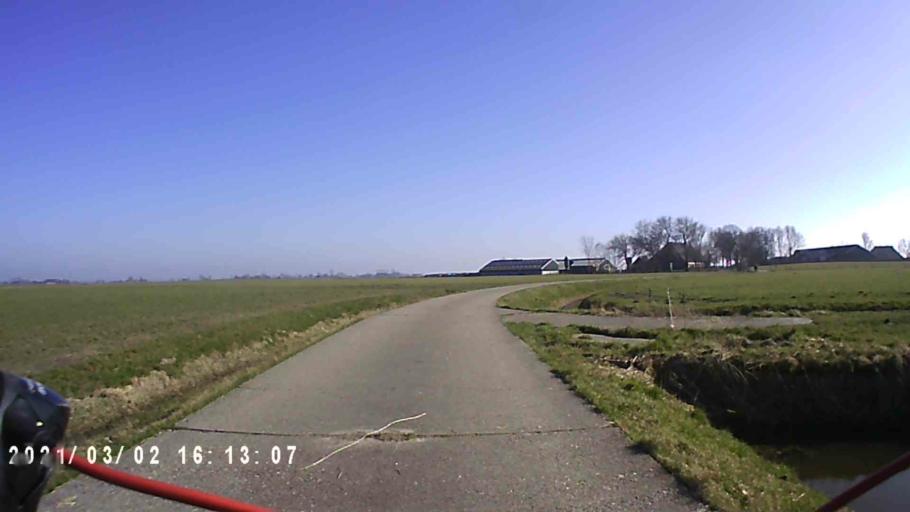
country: NL
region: Groningen
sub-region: Gemeente Zuidhorn
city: Oldehove
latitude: 53.2967
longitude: 6.3985
